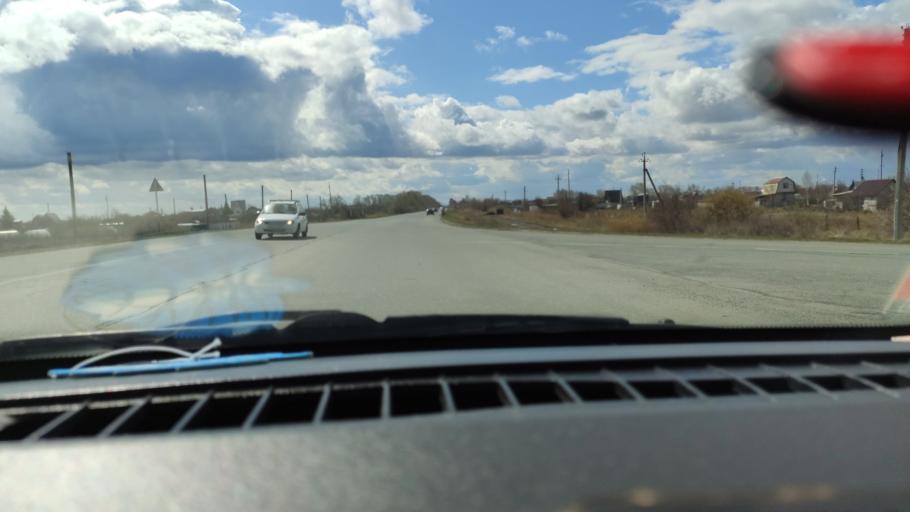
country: RU
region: Samara
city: Tol'yatti
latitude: 53.7094
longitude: 49.4231
